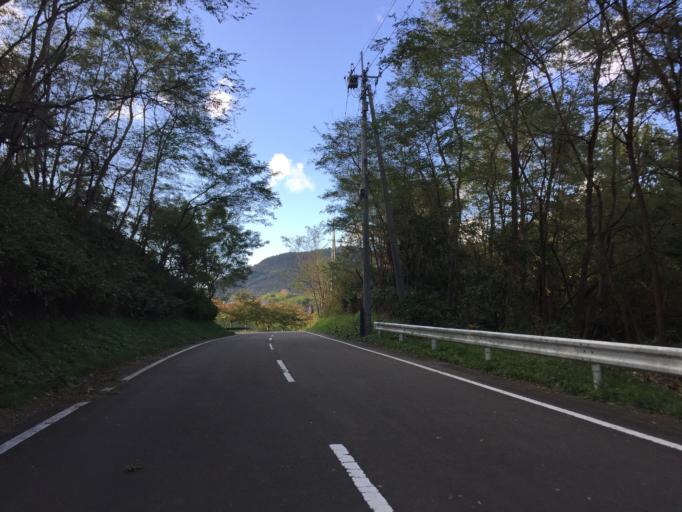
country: JP
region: Fukushima
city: Fukushima-shi
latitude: 37.8382
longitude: 140.4357
